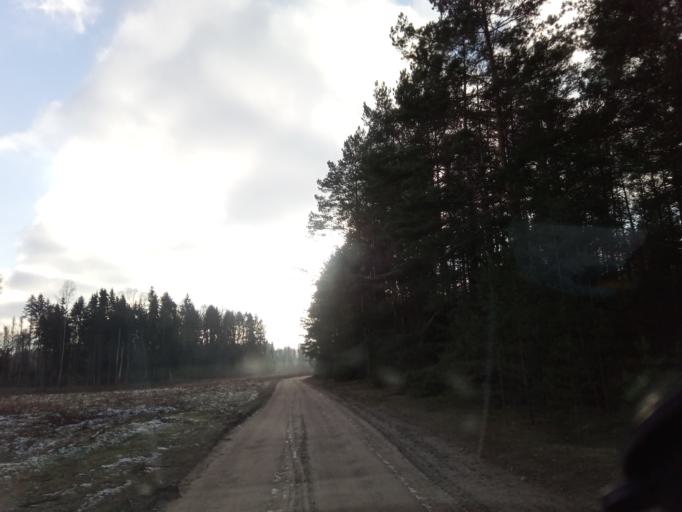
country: LT
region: Alytaus apskritis
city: Druskininkai
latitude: 53.9469
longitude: 24.2832
